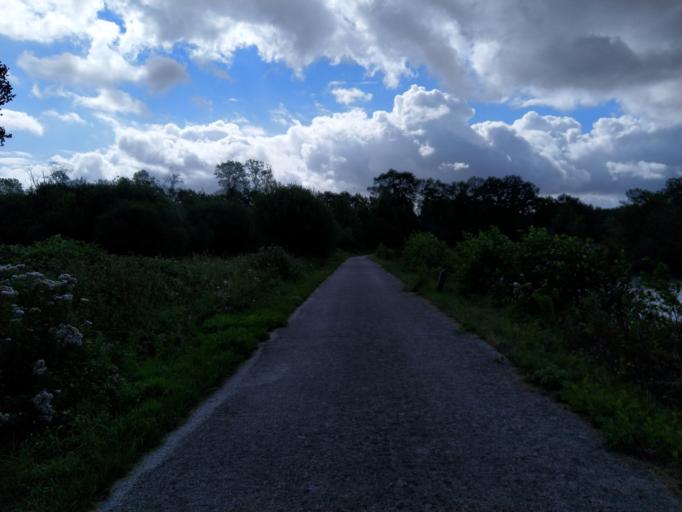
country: BE
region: Wallonia
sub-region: Province du Hainaut
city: Merbes-le-Chateau
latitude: 50.3251
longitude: 4.2172
